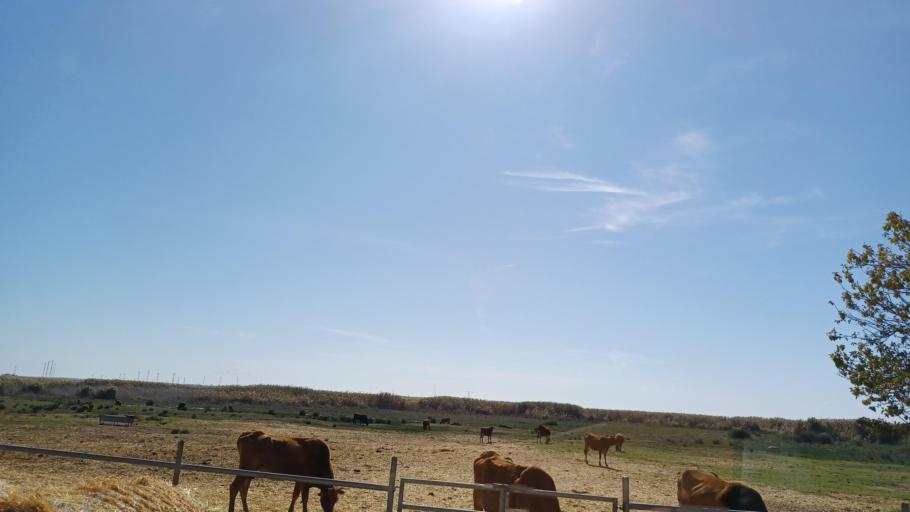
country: CY
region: Larnaka
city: Kolossi
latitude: 34.6335
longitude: 32.9292
